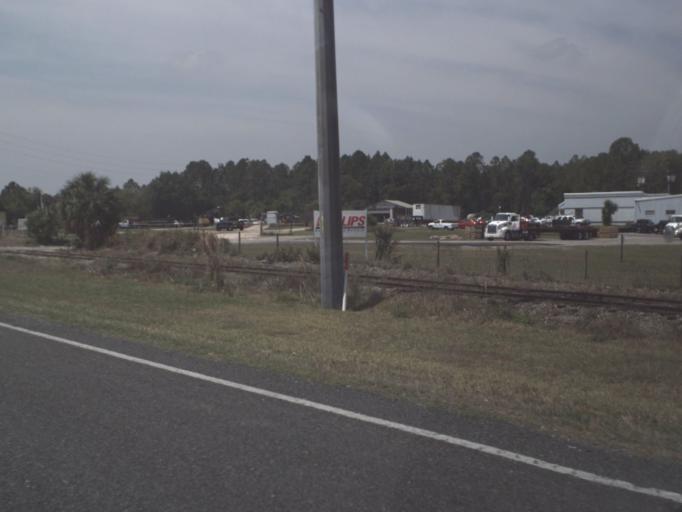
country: US
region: Florida
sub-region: Lake County
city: Umatilla
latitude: 28.9030
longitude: -81.6843
